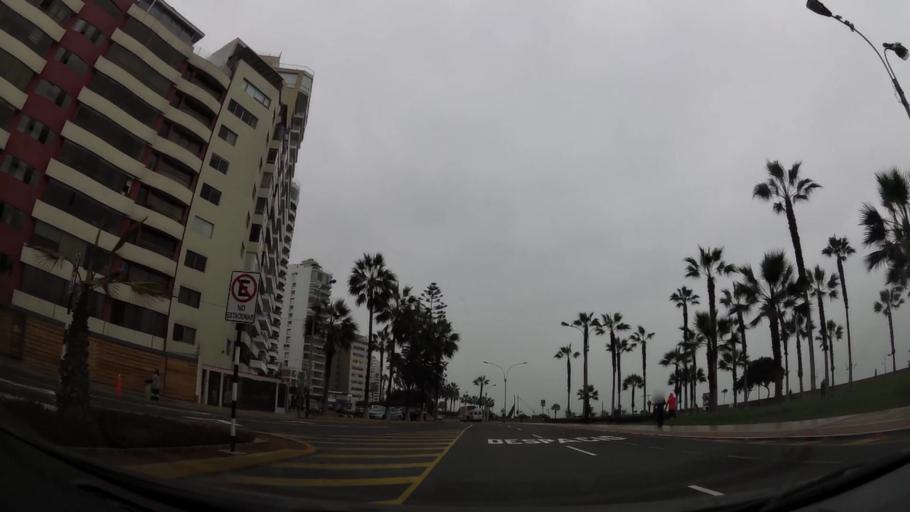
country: PE
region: Lima
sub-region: Lima
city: San Isidro
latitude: -12.1252
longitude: -77.0371
